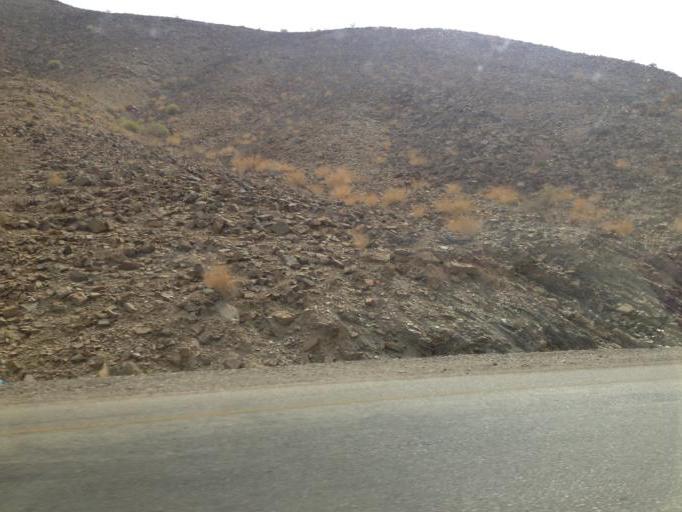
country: OM
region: Ash Sharqiyah
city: Badiyah
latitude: 22.5308
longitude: 58.9648
